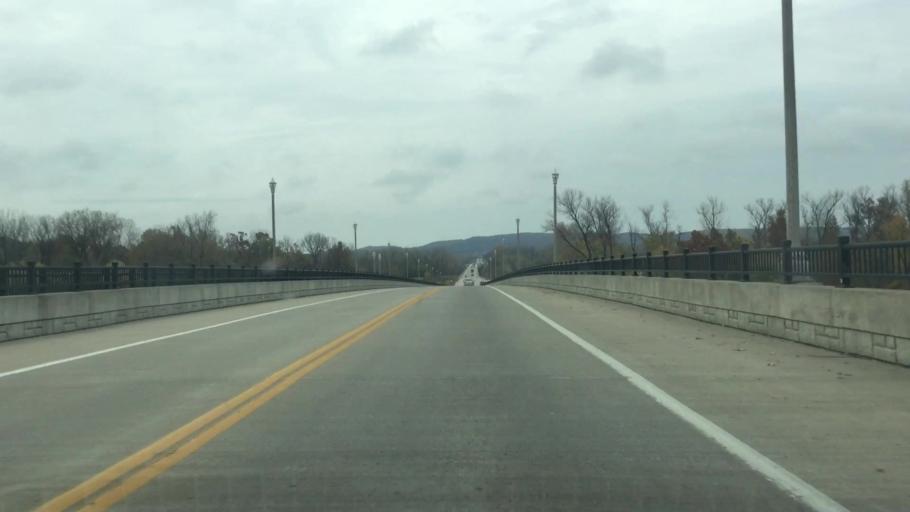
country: US
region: Missouri
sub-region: Gasconade County
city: Hermann
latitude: 38.7099
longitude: -91.4388
